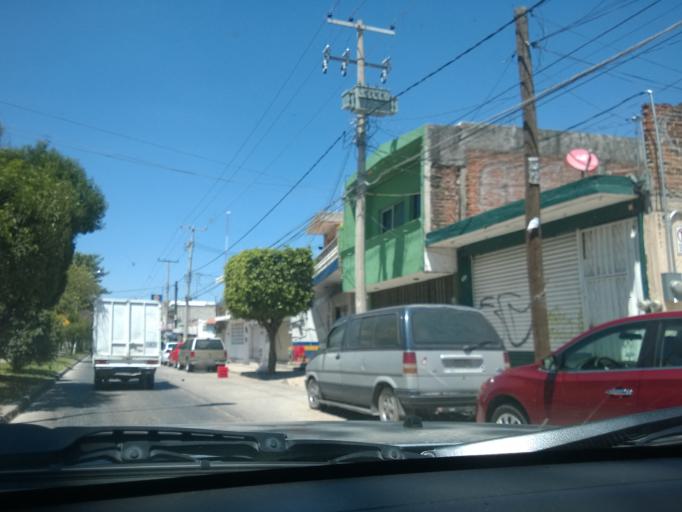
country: MX
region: Guanajuato
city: Leon
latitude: 21.1182
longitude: -101.6414
